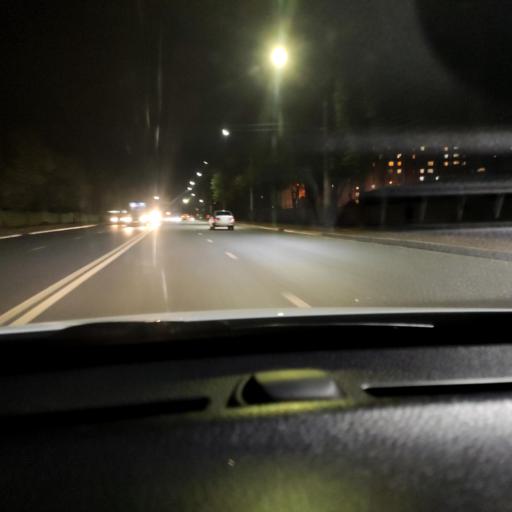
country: RU
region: Voronezj
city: Somovo
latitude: 51.7103
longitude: 39.2762
